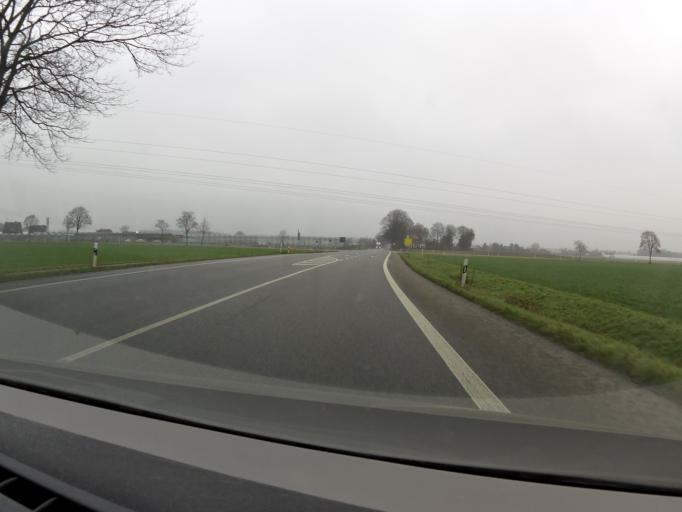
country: DE
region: North Rhine-Westphalia
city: Straelen
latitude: 51.4021
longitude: 6.2605
